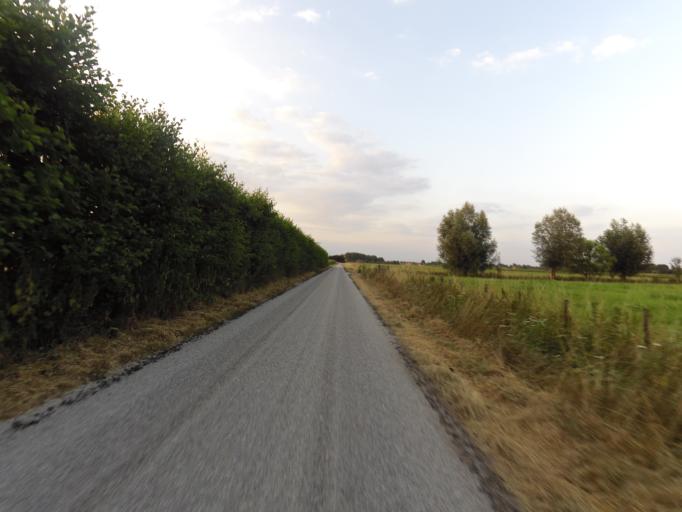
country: NL
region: Gelderland
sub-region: Gemeente Zevenaar
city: Zevenaar
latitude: 51.8849
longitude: 6.0745
